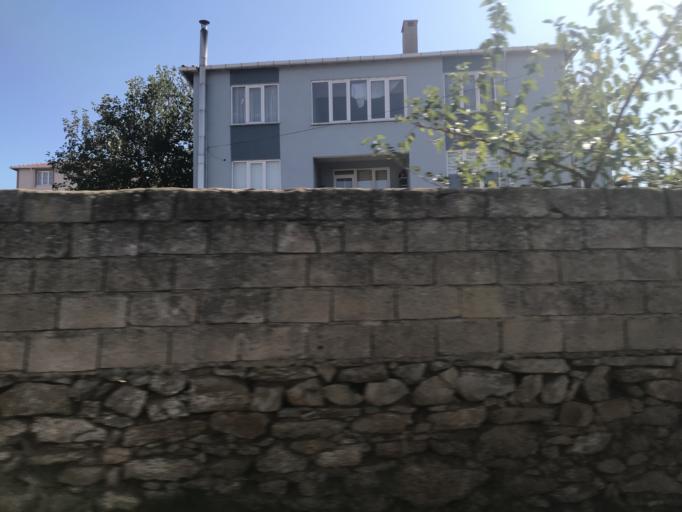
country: TR
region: Kirklareli
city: Kirklareli
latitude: 41.7734
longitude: 27.2263
